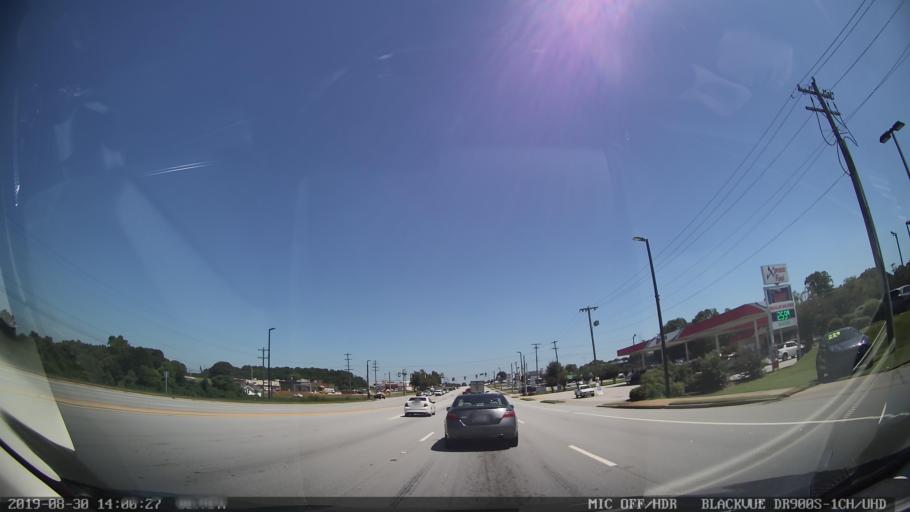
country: US
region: South Carolina
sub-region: Greenville County
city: Greer
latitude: 34.9479
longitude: -82.2163
